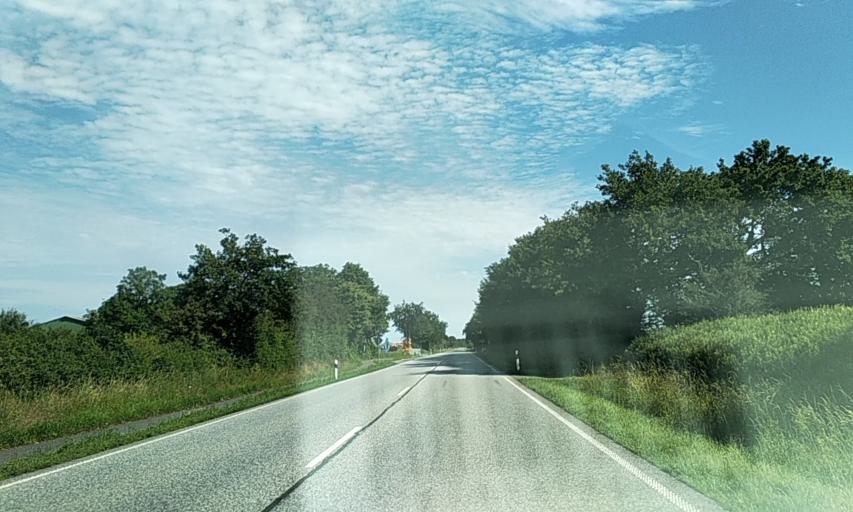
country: DE
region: Schleswig-Holstein
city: Kropp
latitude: 54.4328
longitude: 9.5326
